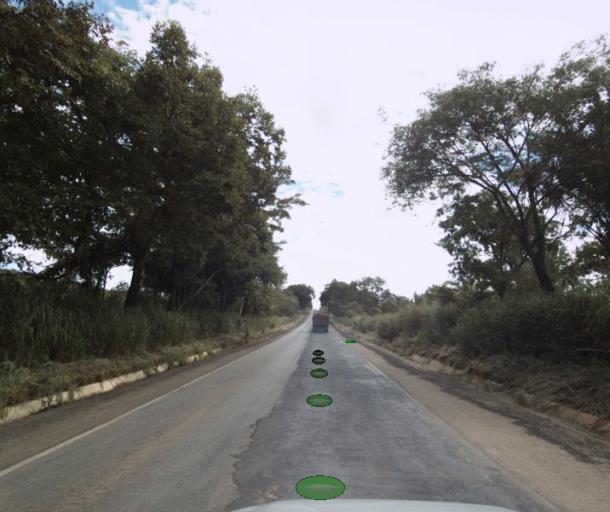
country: BR
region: Goias
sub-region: Uruacu
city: Uruacu
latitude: -14.3926
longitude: -49.1578
